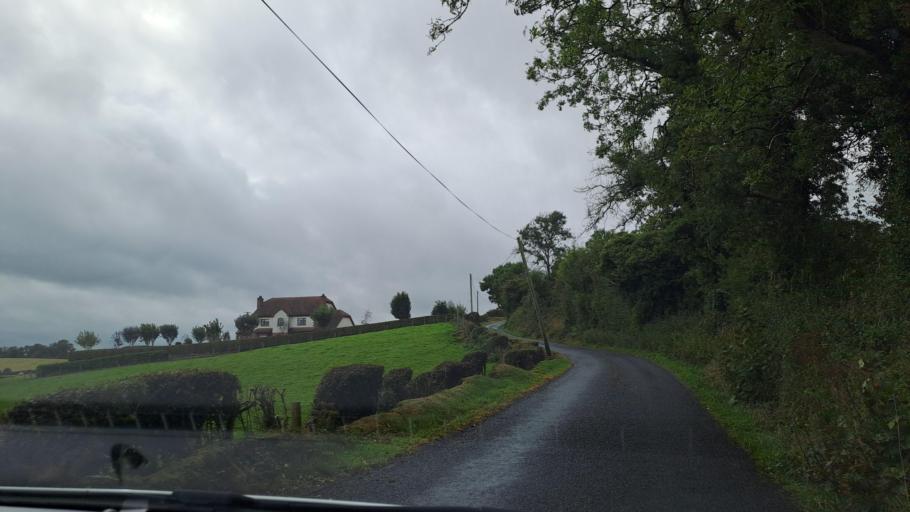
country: IE
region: Ulster
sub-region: An Cabhan
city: Kingscourt
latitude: 53.9414
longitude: -6.8432
